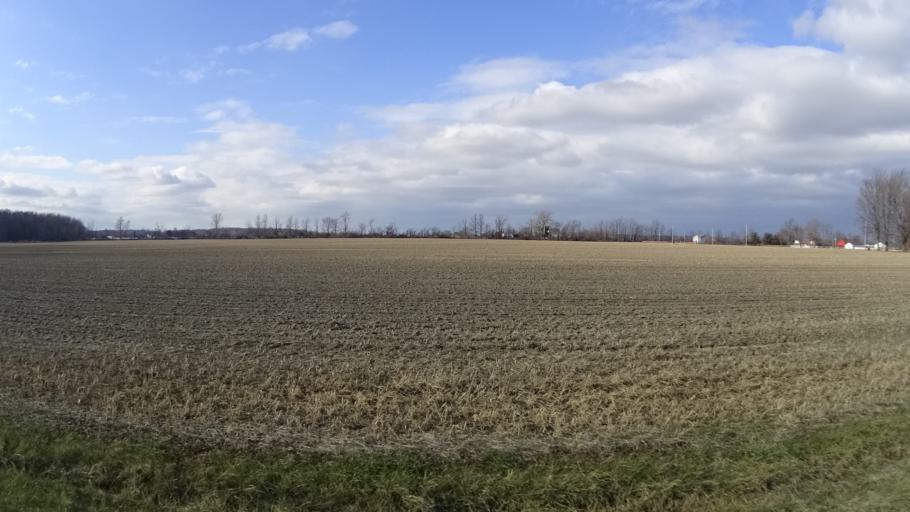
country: US
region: Ohio
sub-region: Lorain County
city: Camden
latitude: 41.2362
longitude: -82.2893
